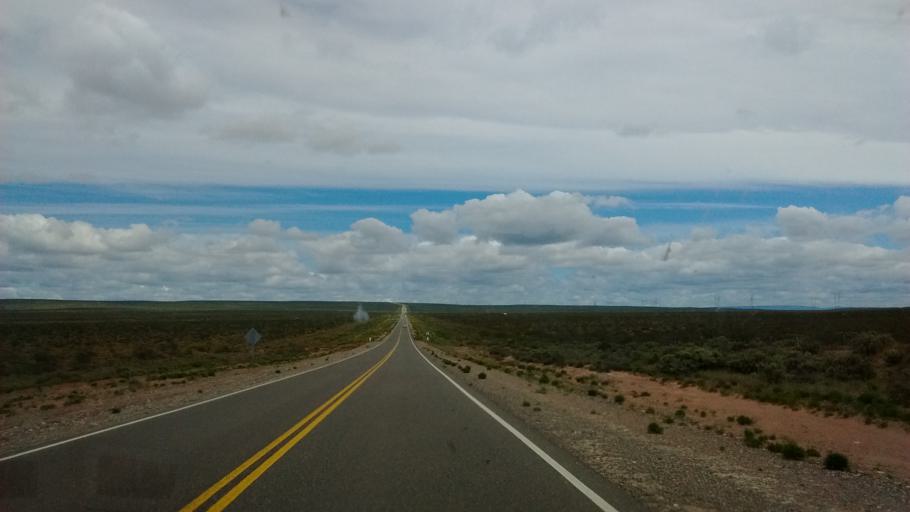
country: AR
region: Neuquen
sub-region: Departamento de Picun Leufu
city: Picun Leufu
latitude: -39.7123
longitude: -69.5159
